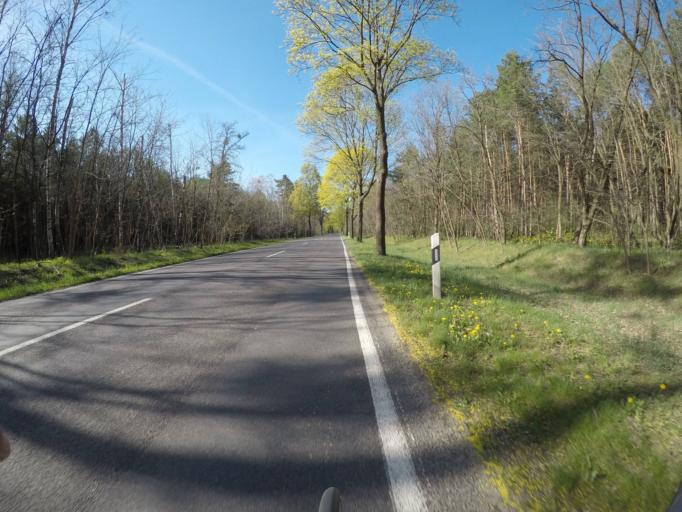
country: DE
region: Brandenburg
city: Grunheide
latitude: 52.4604
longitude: 13.8625
